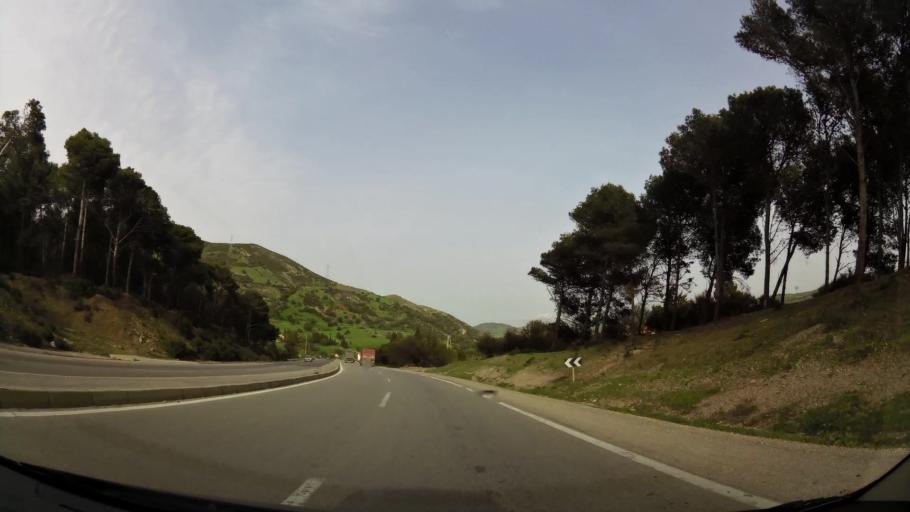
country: MA
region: Tanger-Tetouan
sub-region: Tetouan
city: Saddina
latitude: 35.5497
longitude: -5.5470
